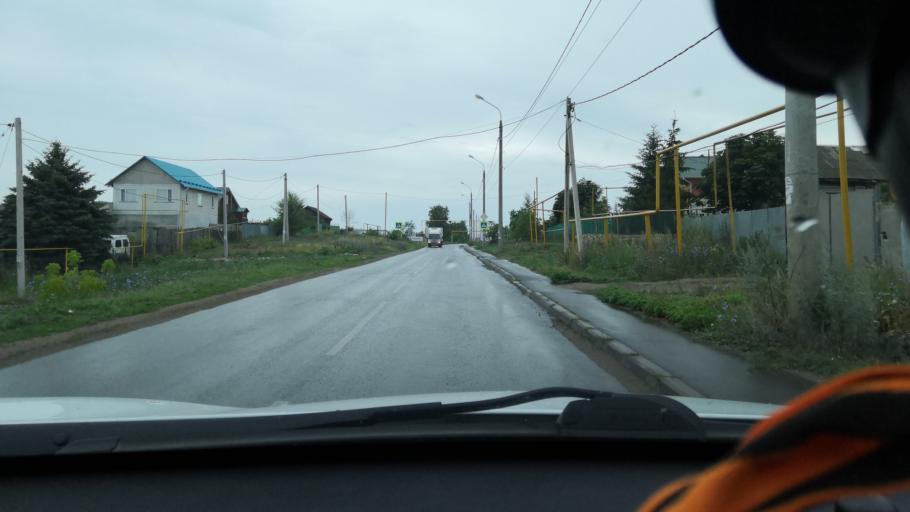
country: RU
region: Samara
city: Novosemeykino
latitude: 53.3815
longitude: 50.3494
